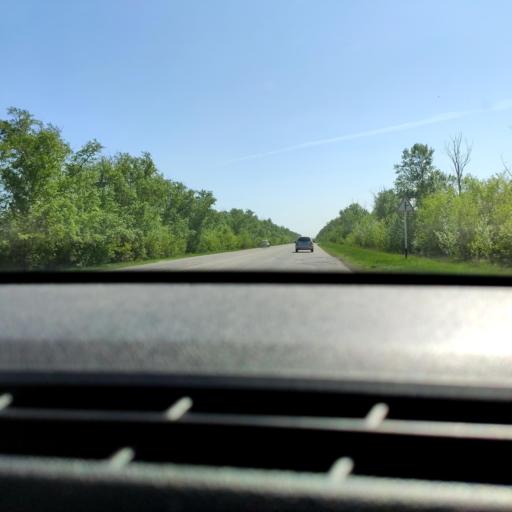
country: RU
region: Samara
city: Tol'yatti
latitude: 53.6071
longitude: 49.4107
